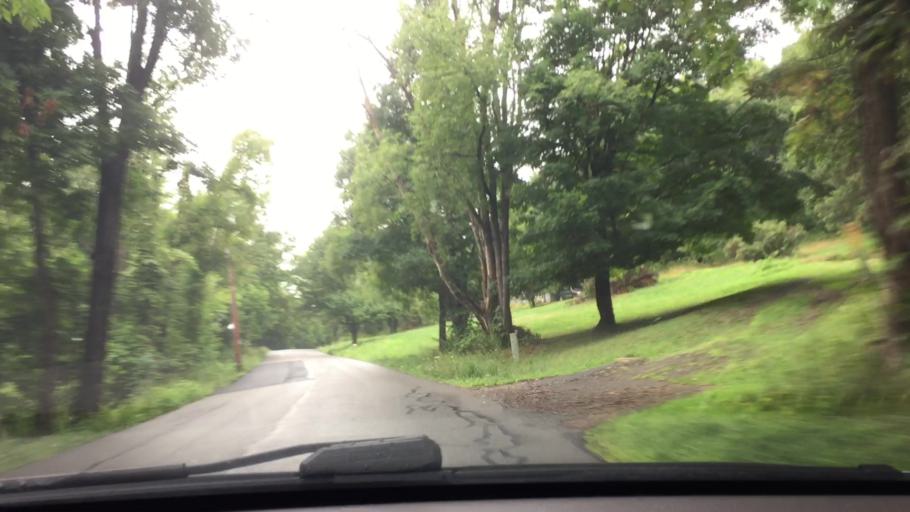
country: US
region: Pennsylvania
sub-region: Washington County
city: Muse
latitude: 40.3004
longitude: -80.1934
